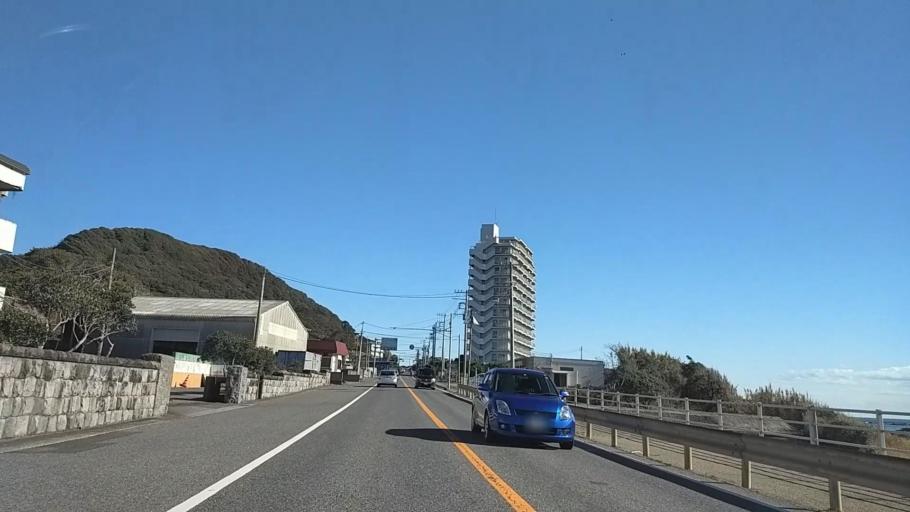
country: JP
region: Chiba
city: Kawaguchi
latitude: 35.0594
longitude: 140.0660
